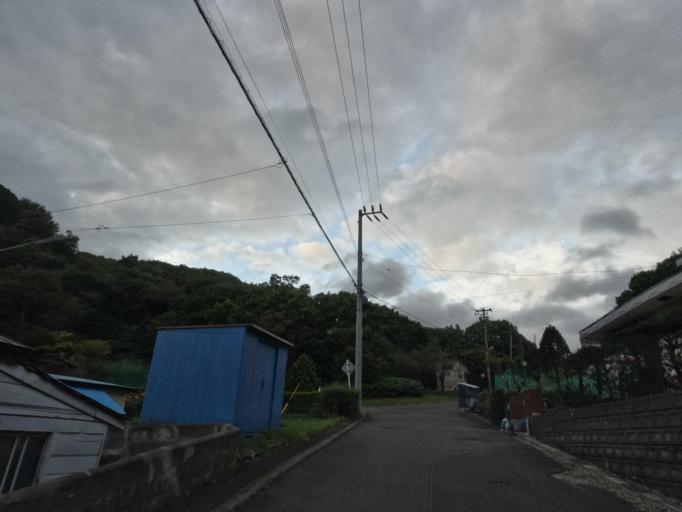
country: JP
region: Hokkaido
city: Muroran
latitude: 42.3668
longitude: 140.9653
